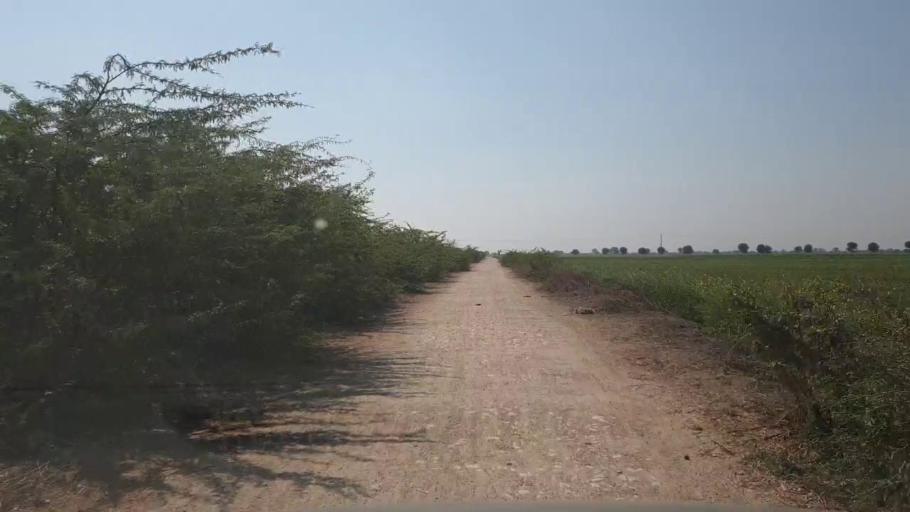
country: PK
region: Sindh
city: Digri
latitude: 25.2358
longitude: 69.2238
